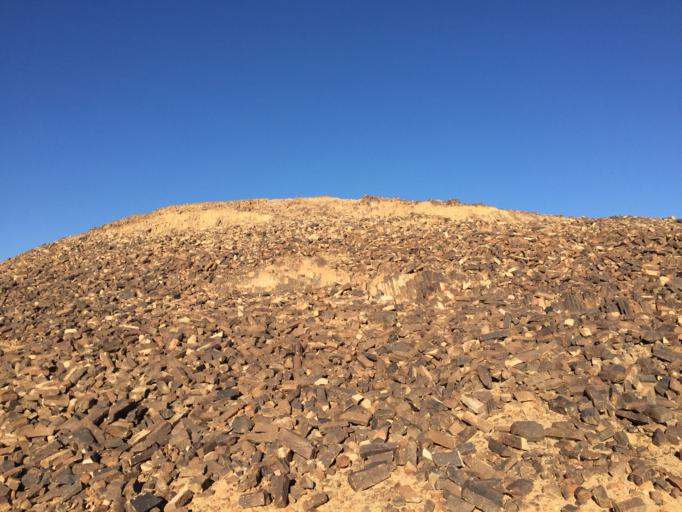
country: IL
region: Southern District
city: Mitzpe Ramon
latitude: 30.6153
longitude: 34.8392
